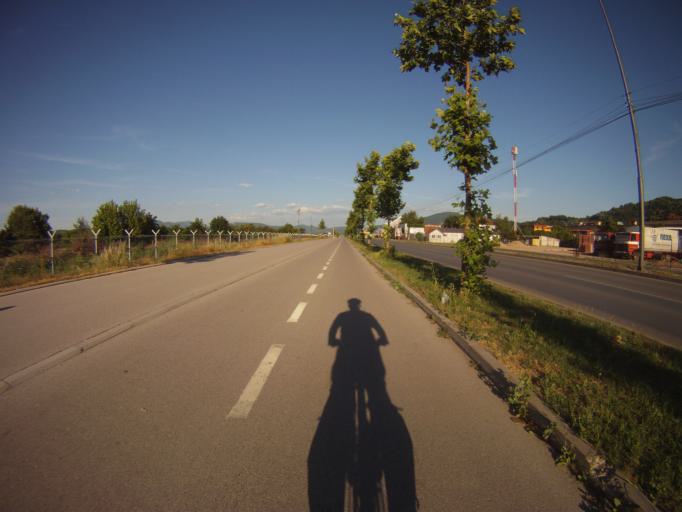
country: RS
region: Central Serbia
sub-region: Nisavski Okrug
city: Nis
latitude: 43.3094
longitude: 21.9415
